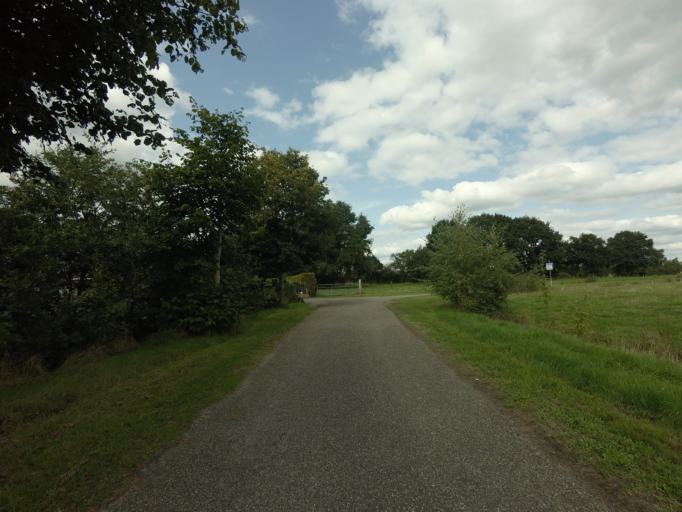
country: NL
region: Drenthe
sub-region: Gemeente De Wolden
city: Ruinen
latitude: 52.7059
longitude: 6.3232
